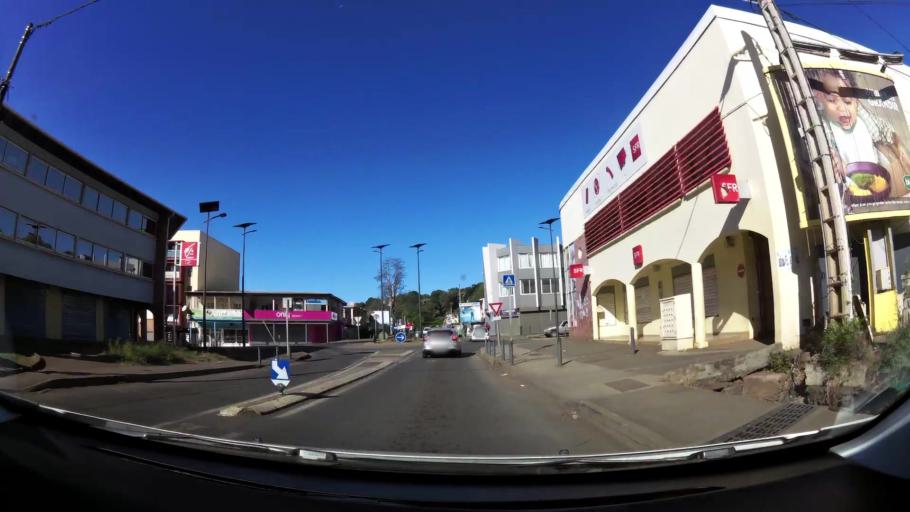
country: YT
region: Mamoudzou
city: Mamoudzou
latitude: -12.7758
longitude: 45.2242
